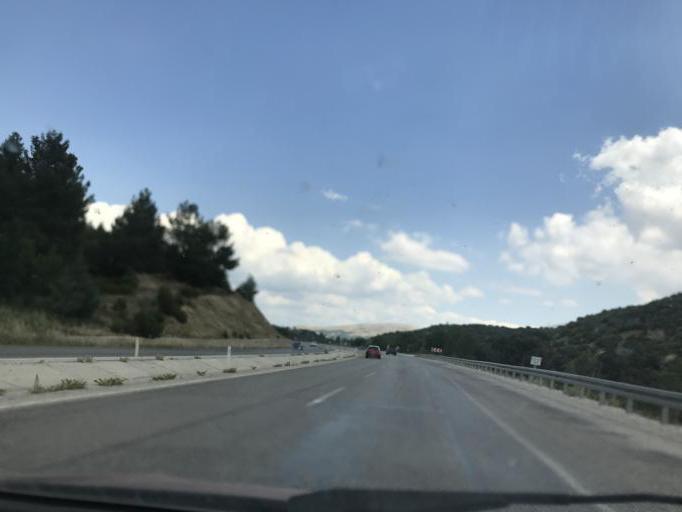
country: TR
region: Denizli
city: Tavas
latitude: 37.6135
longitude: 29.1519
